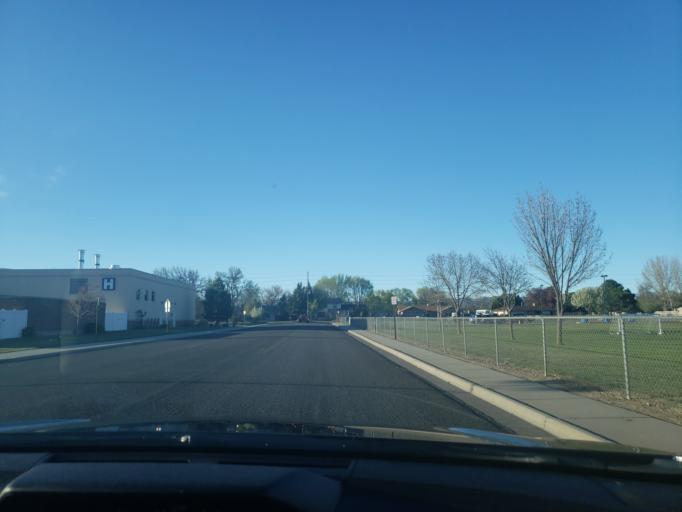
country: US
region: Colorado
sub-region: Mesa County
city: Fruita
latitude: 39.1630
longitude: -108.7359
